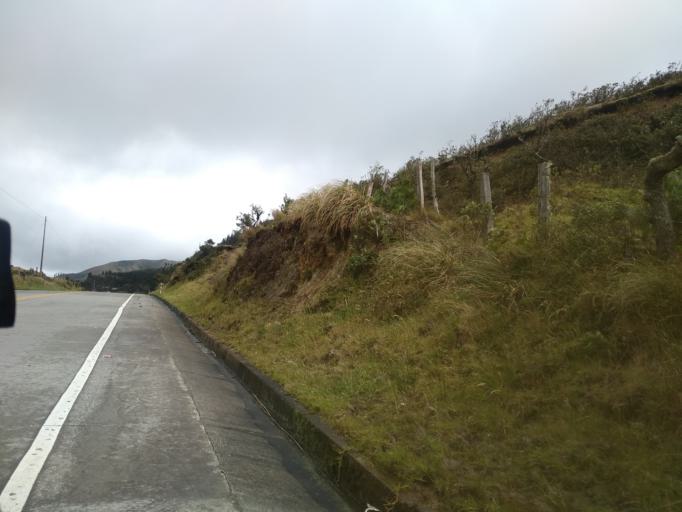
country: EC
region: Loja
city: Loja
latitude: -3.8858
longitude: -79.2631
